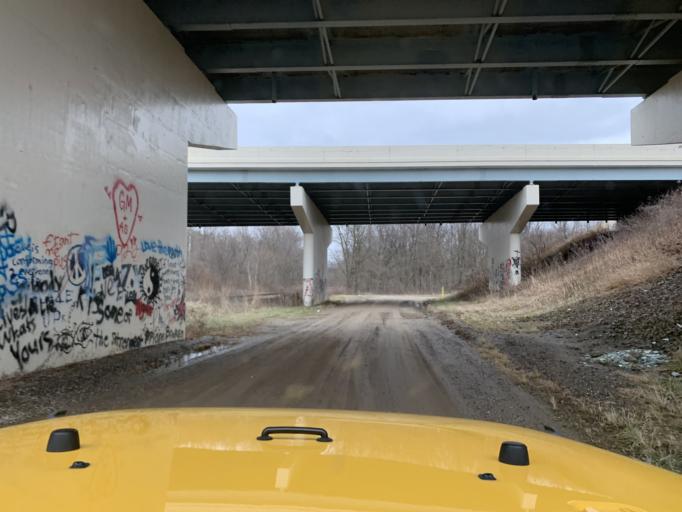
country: US
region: Ohio
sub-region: Tuscarawas County
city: Newcomerstown
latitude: 40.2876
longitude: -81.5558
